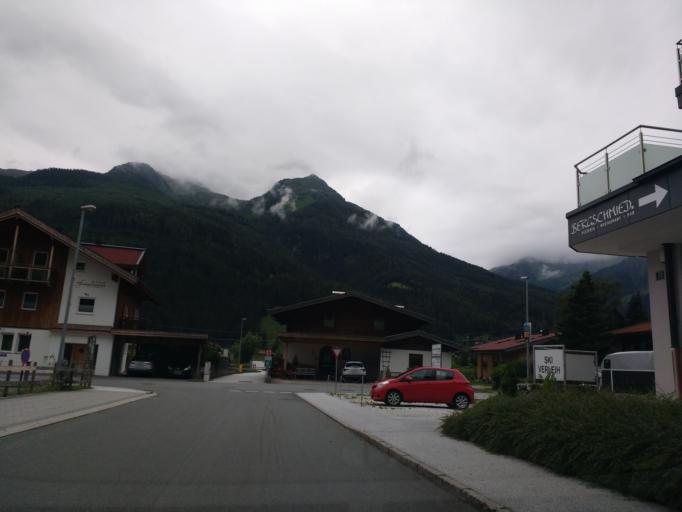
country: AT
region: Salzburg
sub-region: Politischer Bezirk Zell am See
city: Bramberg am Wildkogel
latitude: 47.2717
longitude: 12.3406
